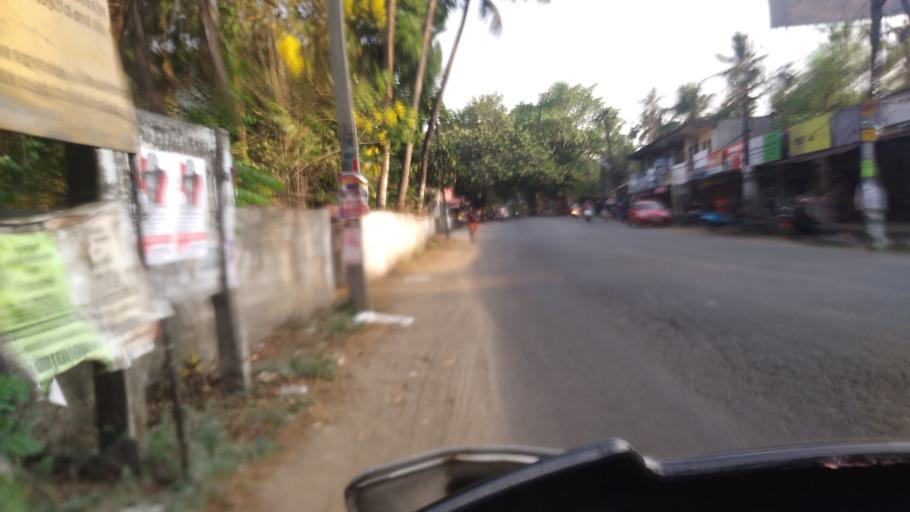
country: IN
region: Kerala
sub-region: Thrissur District
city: Thanniyam
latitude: 10.3850
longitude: 76.1202
